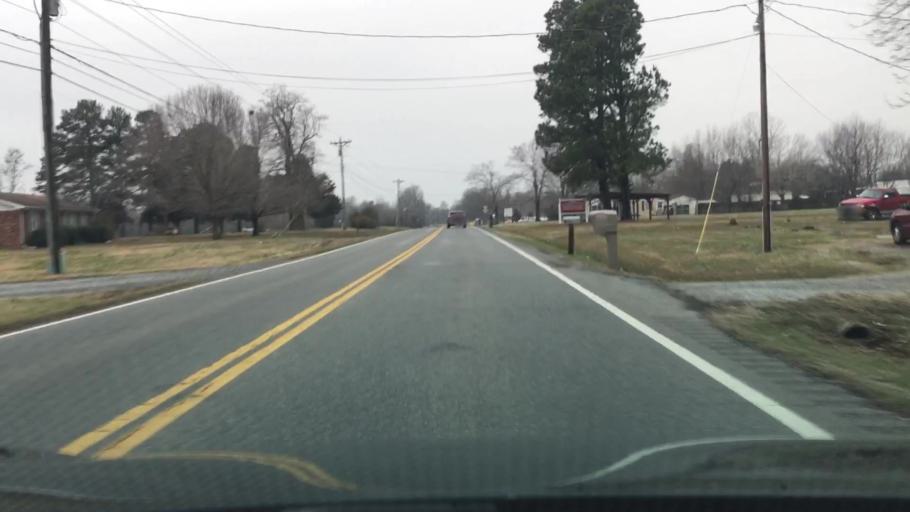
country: US
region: Kentucky
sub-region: Marshall County
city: Calvert City
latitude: 36.9720
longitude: -88.3937
